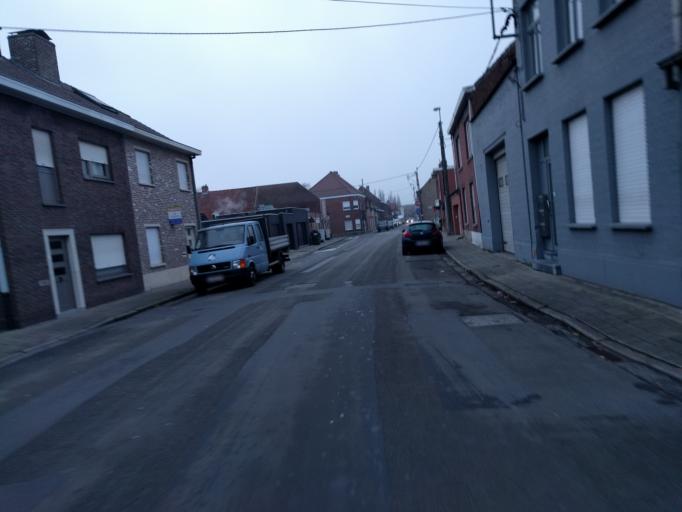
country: BE
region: Flanders
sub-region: Provincie West-Vlaanderen
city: Kortrijk
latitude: 50.8272
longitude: 3.2293
